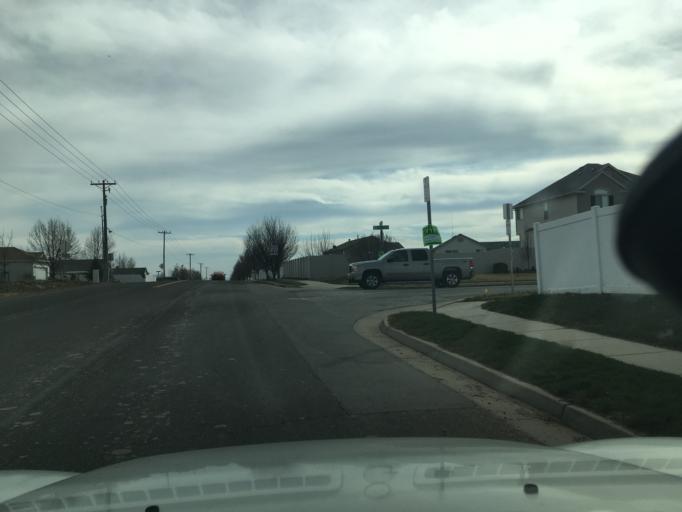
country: US
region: Utah
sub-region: Davis County
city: Clearfield
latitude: 41.0825
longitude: -112.0070
